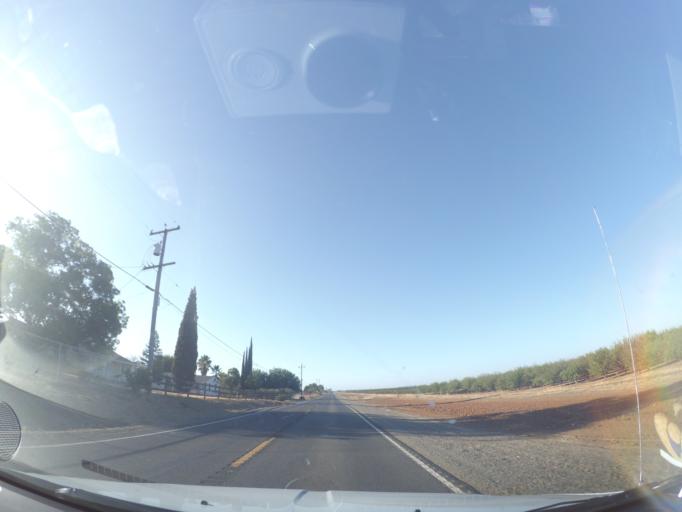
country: US
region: California
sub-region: Merced County
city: Merced
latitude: 37.3820
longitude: -120.5032
